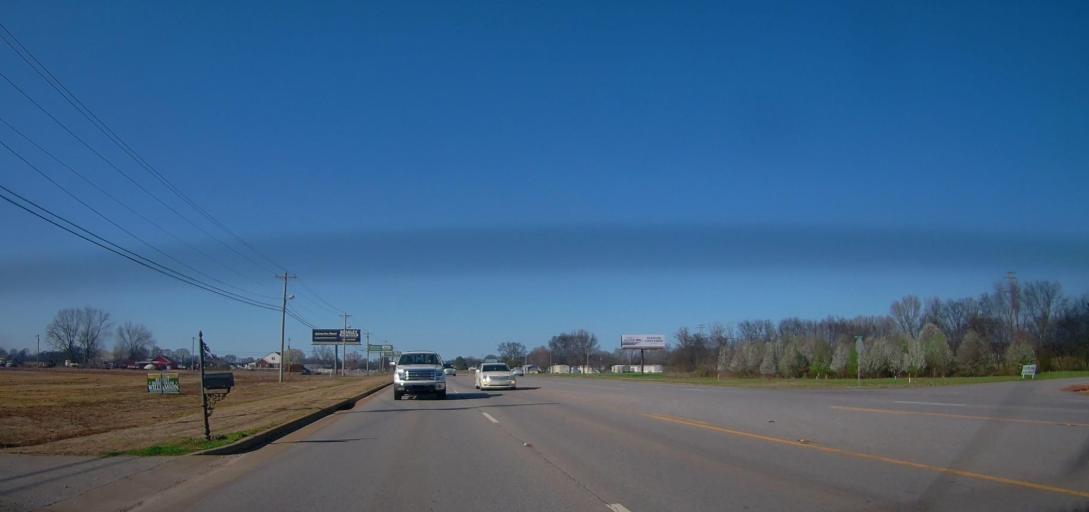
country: US
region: Alabama
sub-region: Colbert County
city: Muscle Shoals
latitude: 34.7174
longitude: -87.6350
